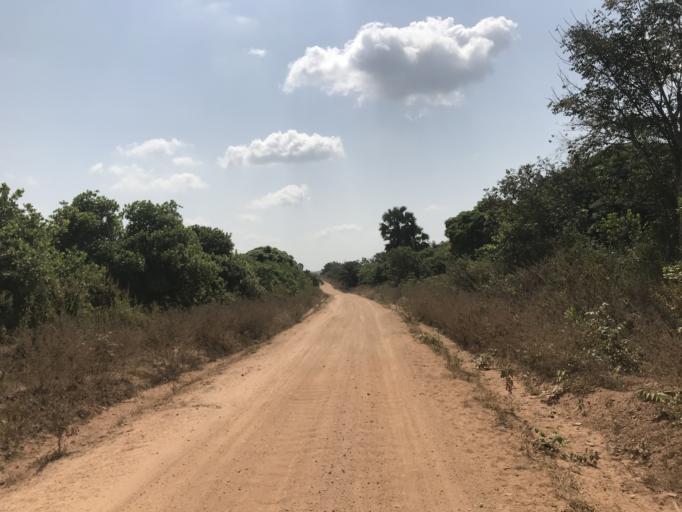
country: NG
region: Osun
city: Ifon
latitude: 7.9408
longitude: 4.4870
